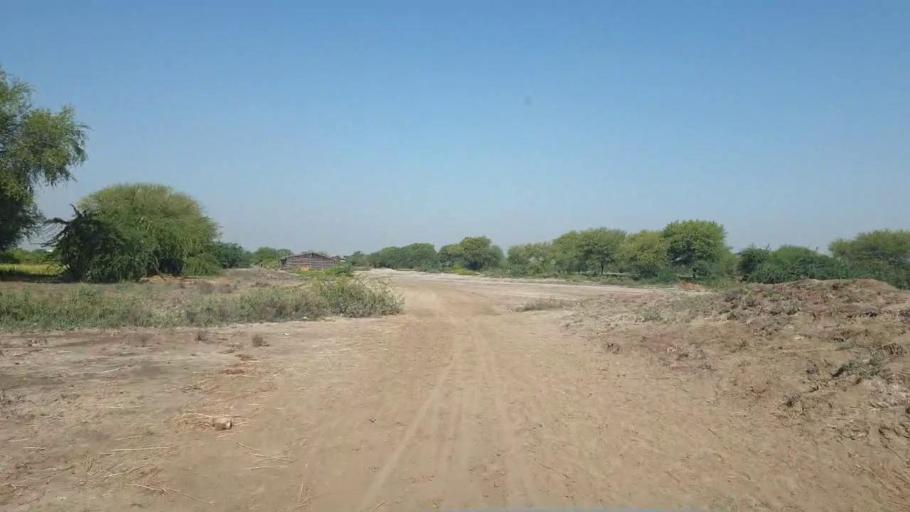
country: PK
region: Sindh
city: Talhar
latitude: 24.8121
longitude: 68.7842
